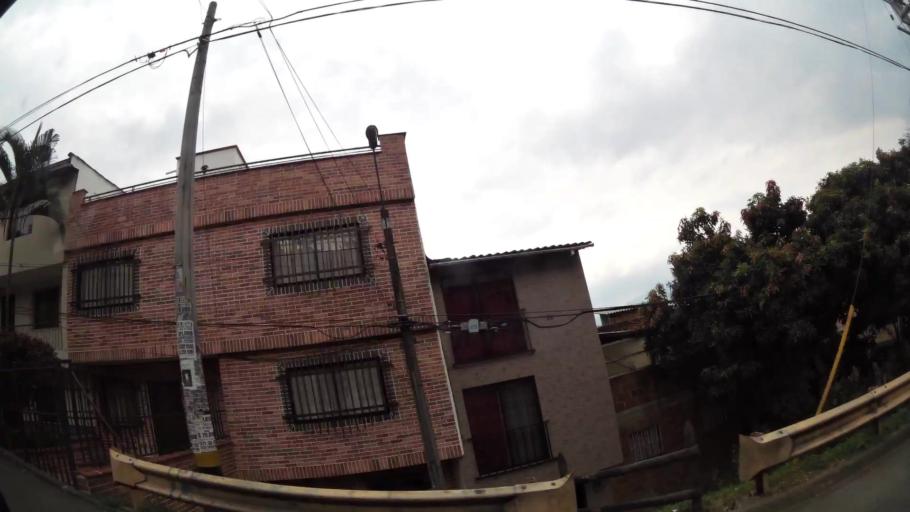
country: CO
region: Antioquia
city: Medellin
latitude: 6.2488
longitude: -75.5479
